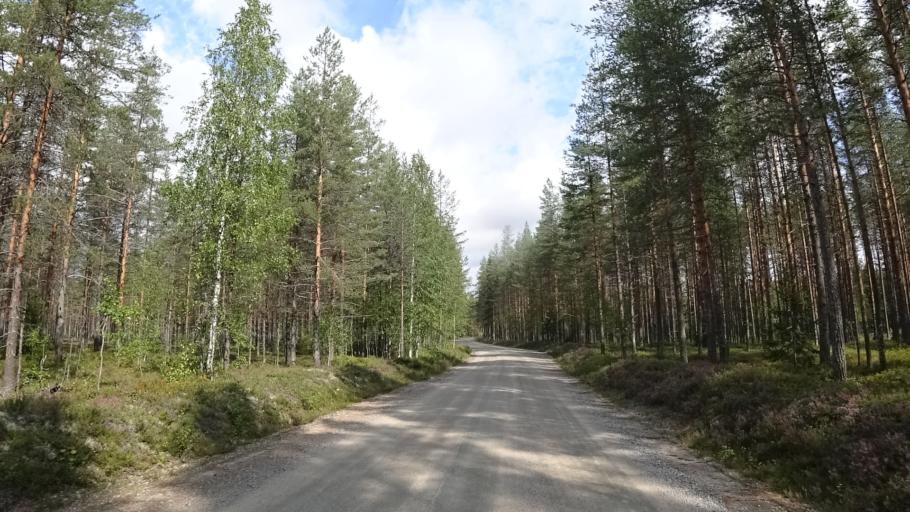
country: FI
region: North Karelia
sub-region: Joensuu
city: Ilomantsi
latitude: 62.9377
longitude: 31.4333
